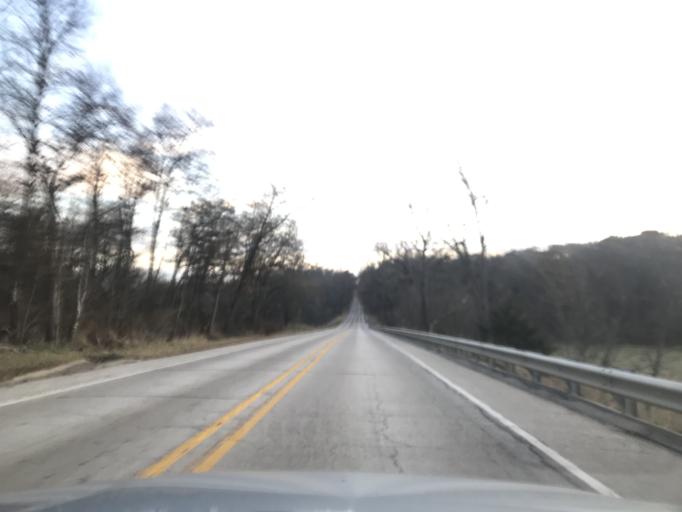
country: US
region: Illinois
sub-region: Henderson County
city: Oquawka
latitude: 40.9051
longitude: -90.8644
